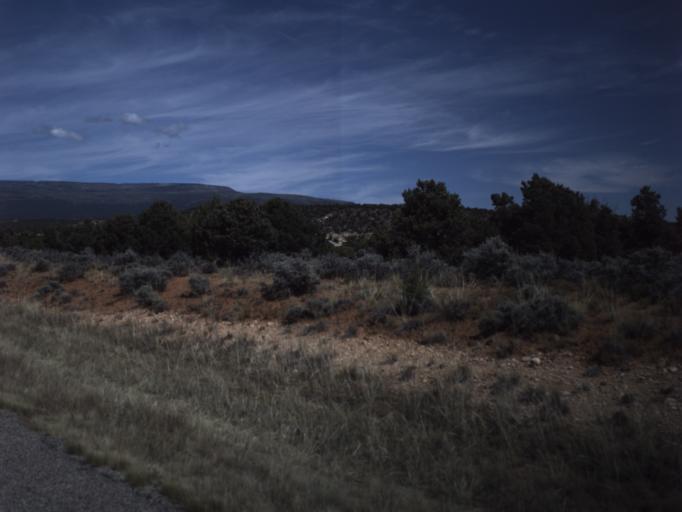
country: US
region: Utah
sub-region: Wayne County
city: Loa
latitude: 37.8870
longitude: -111.4580
